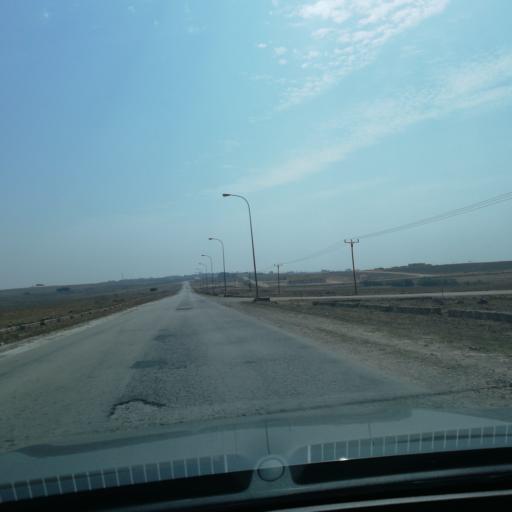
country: OM
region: Zufar
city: Salalah
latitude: 17.2409
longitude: 54.0611
